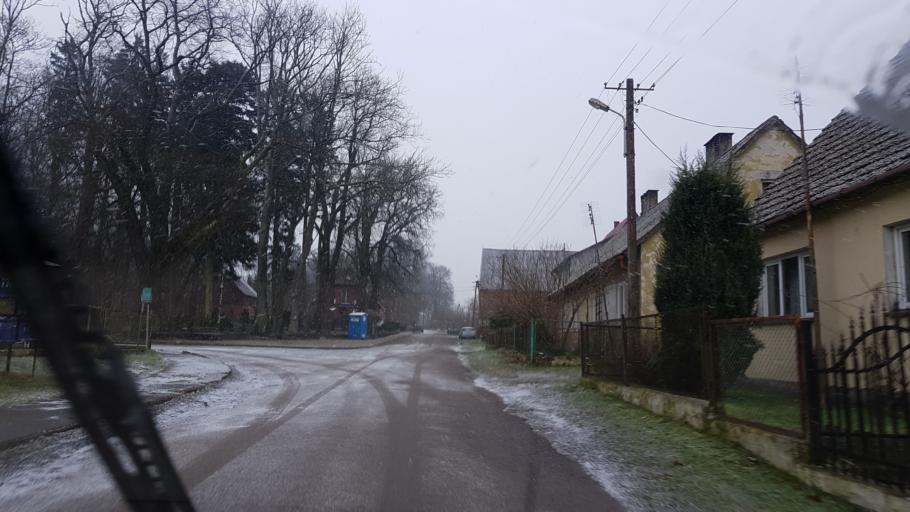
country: PL
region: West Pomeranian Voivodeship
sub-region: Powiat slawienski
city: Slawno
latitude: 54.2822
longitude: 16.6003
